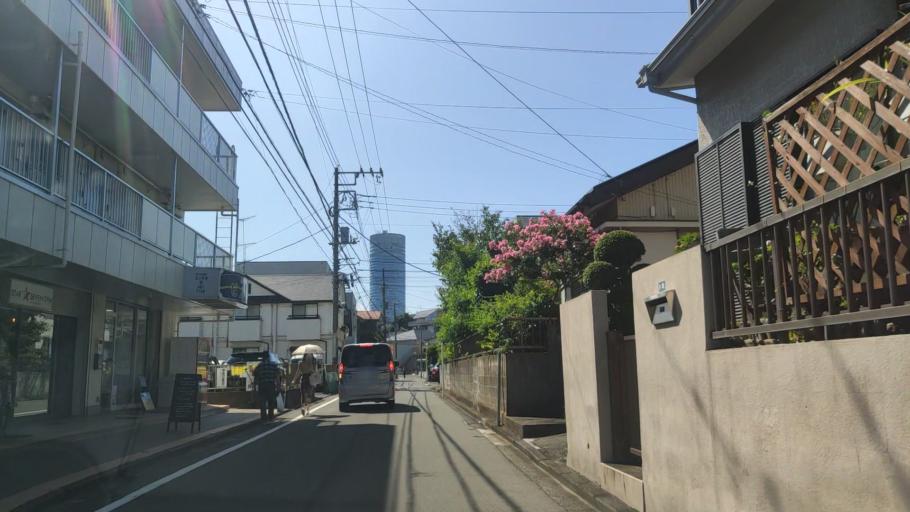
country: JP
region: Kanagawa
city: Yokohama
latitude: 35.5099
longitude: 139.6277
